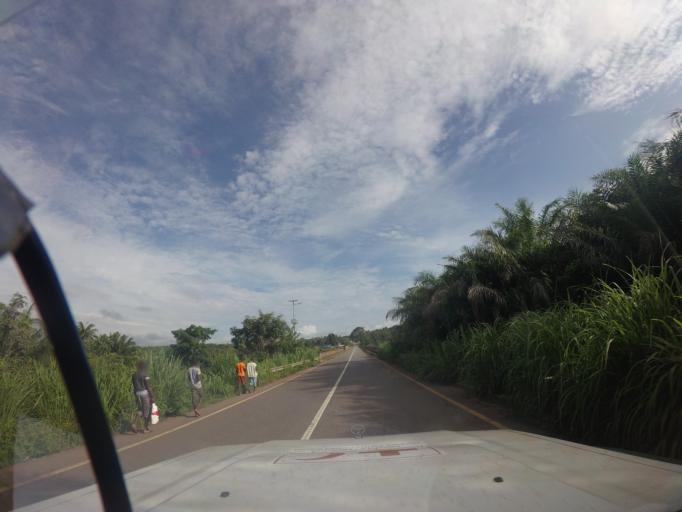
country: SL
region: Northern Province
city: Kambia
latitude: 9.1174
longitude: -12.9304
